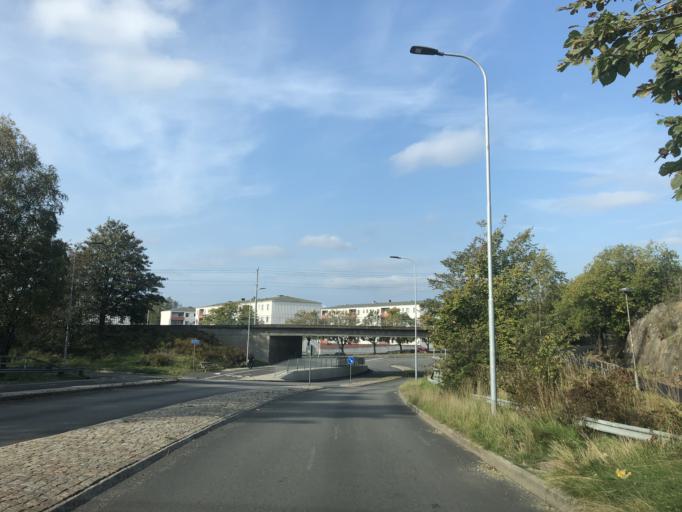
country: SE
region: Vaestra Goetaland
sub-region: Goteborg
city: Majorna
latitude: 57.6469
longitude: 11.9039
